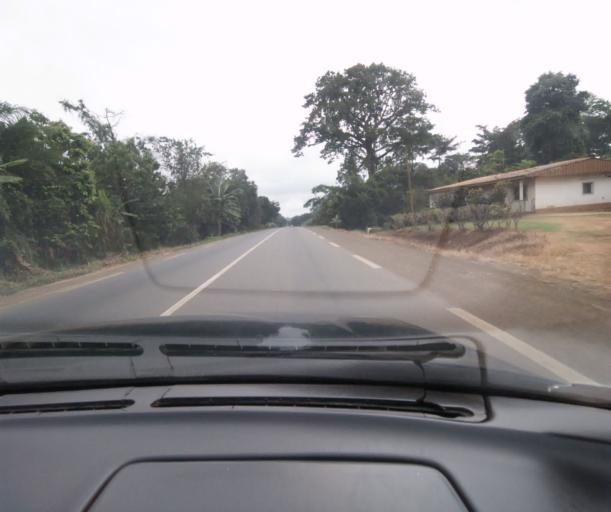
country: CM
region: Centre
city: Obala
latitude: 4.1148
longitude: 11.5274
